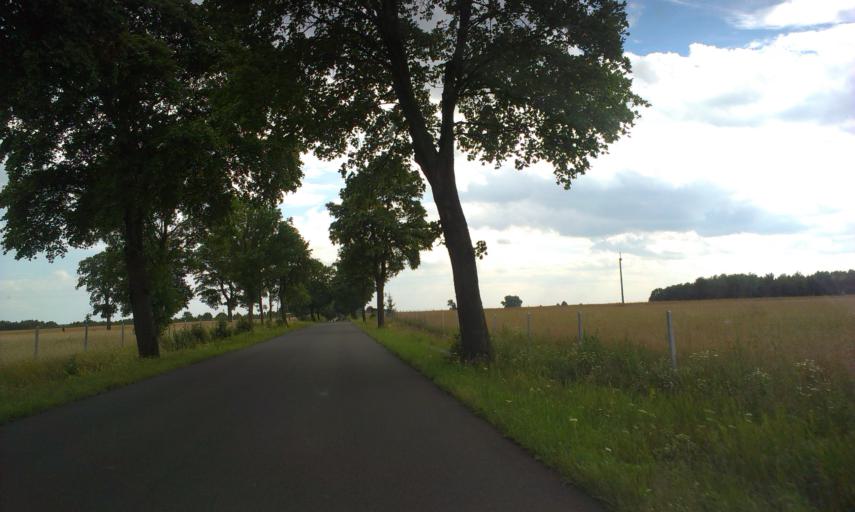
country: PL
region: Greater Poland Voivodeship
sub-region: Powiat zlotowski
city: Zlotow
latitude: 53.4696
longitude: 16.9893
